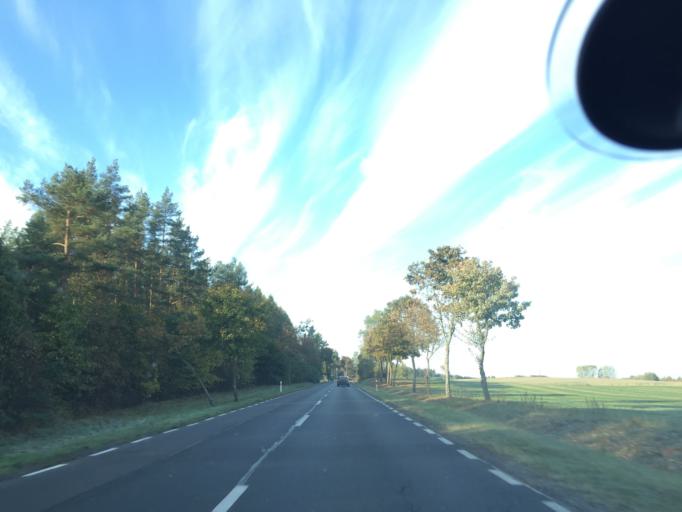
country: PL
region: Warmian-Masurian Voivodeship
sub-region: Powiat lidzbarski
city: Lidzbark Warminski
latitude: 54.1587
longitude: 20.6335
